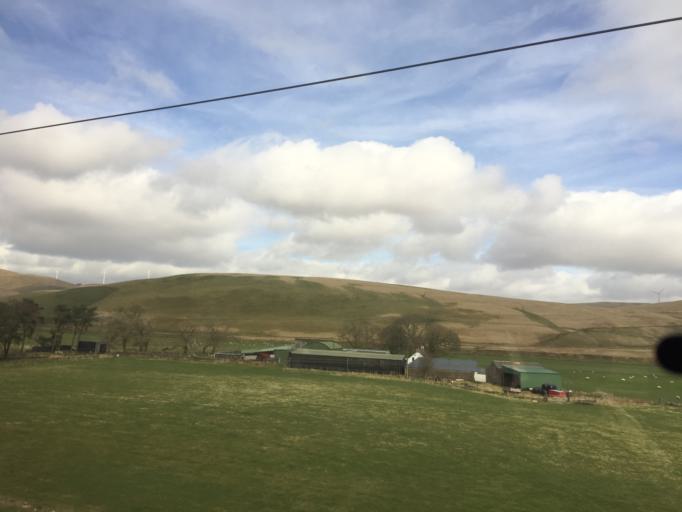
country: GB
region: Scotland
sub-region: South Lanarkshire
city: Biggar
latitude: 55.4649
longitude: -3.6459
